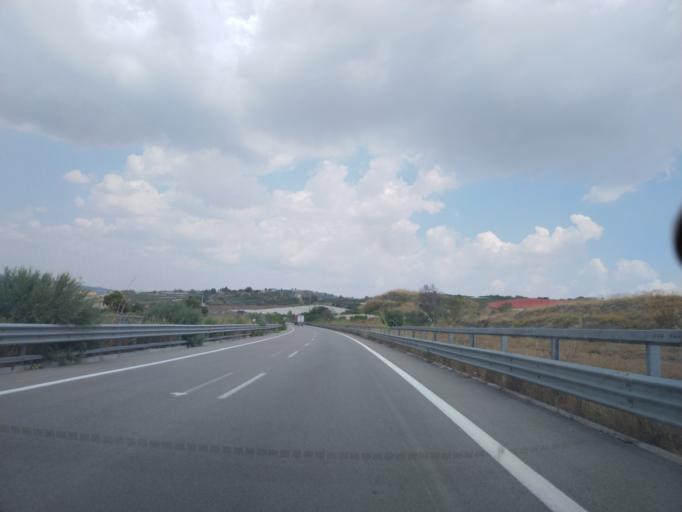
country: IT
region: Sicily
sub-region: Agrigento
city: Canicatti
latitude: 37.3833
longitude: 13.8216
